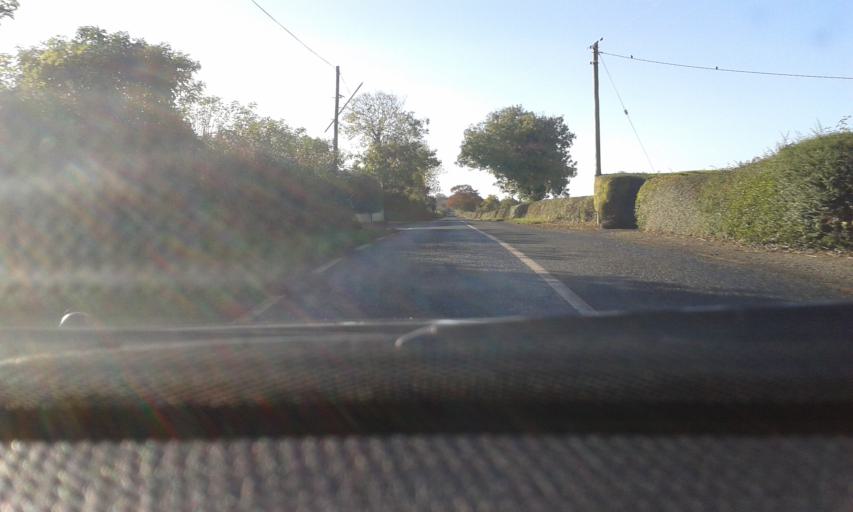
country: IE
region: Leinster
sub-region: Kildare
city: Rathangan
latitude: 53.1820
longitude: -7.0191
